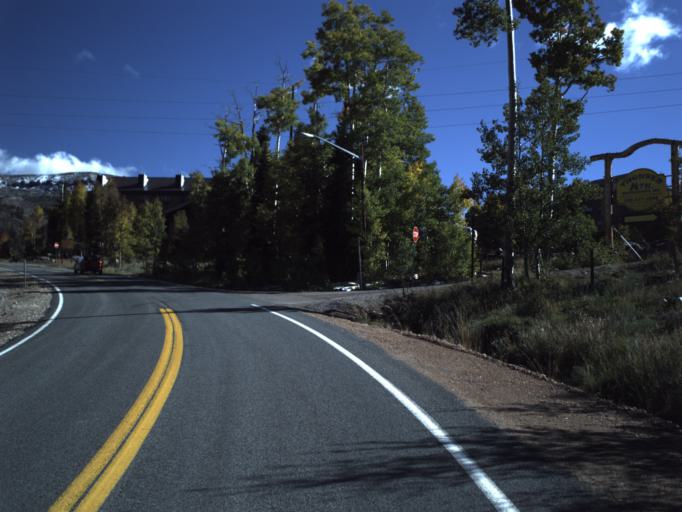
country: US
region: Utah
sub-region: Iron County
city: Parowan
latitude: 37.7069
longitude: -112.8507
